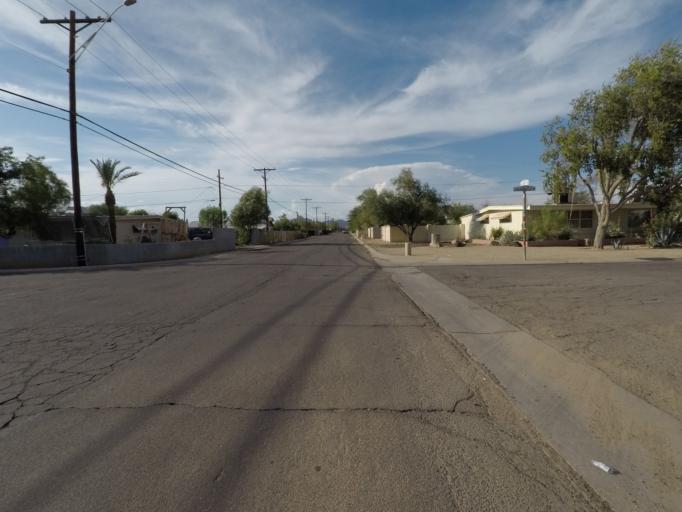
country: US
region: Arizona
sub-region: Maricopa County
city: Phoenix
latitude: 33.4701
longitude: -112.0085
